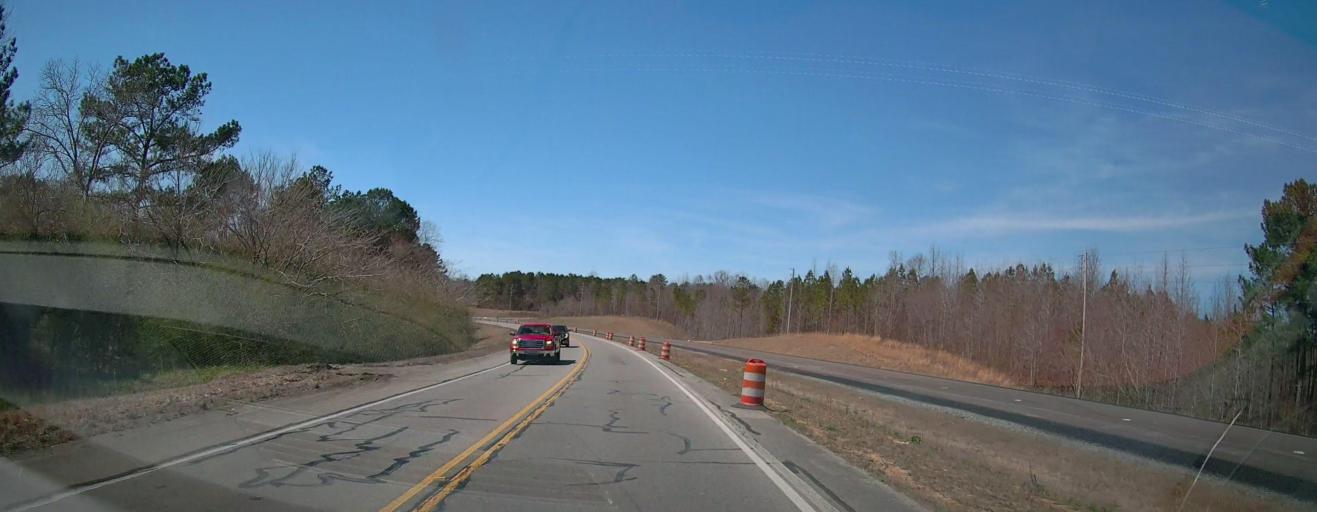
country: US
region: Alabama
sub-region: Cullman County
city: Cullman
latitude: 34.1975
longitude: -86.7912
